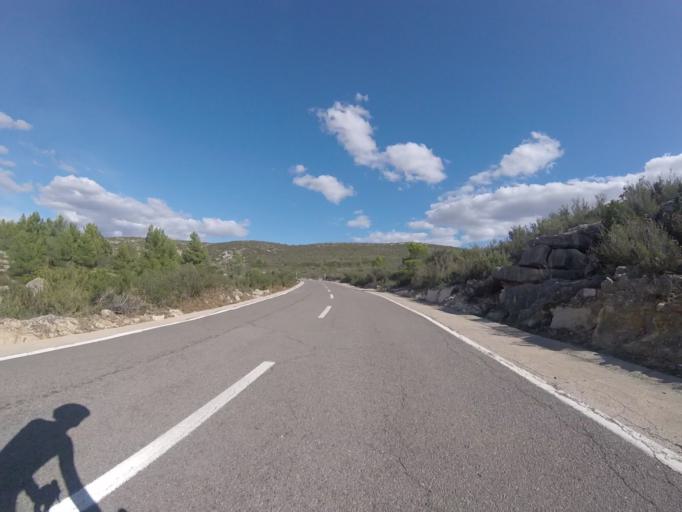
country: ES
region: Valencia
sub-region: Provincia de Castello
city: Alcala de Xivert
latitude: 40.2949
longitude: 0.1782
